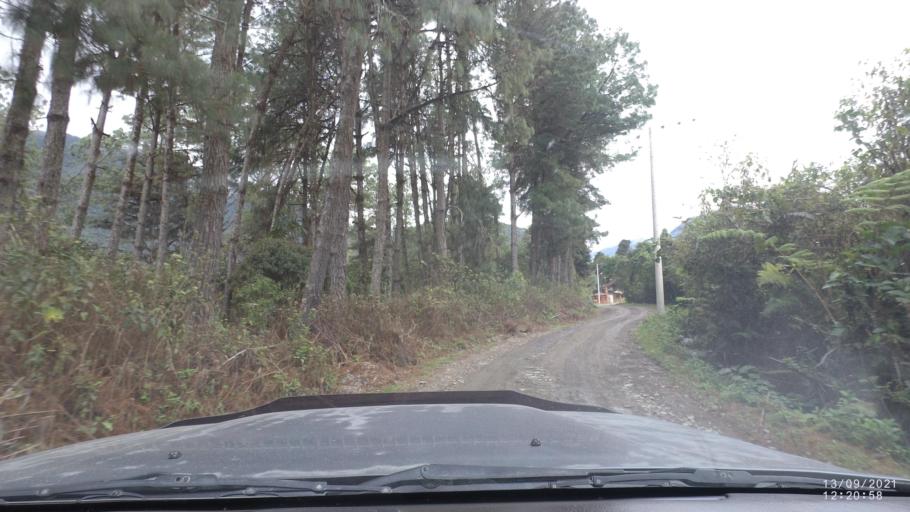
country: BO
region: Cochabamba
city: Colomi
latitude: -17.2356
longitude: -65.8175
